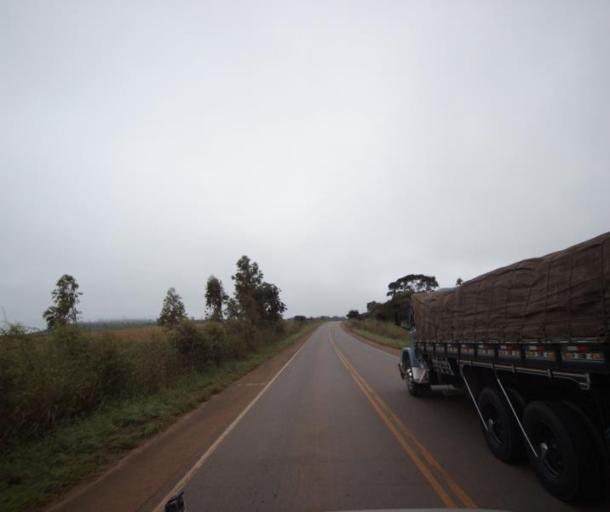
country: BR
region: Goias
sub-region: Pirenopolis
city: Pirenopolis
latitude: -15.9677
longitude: -48.8226
